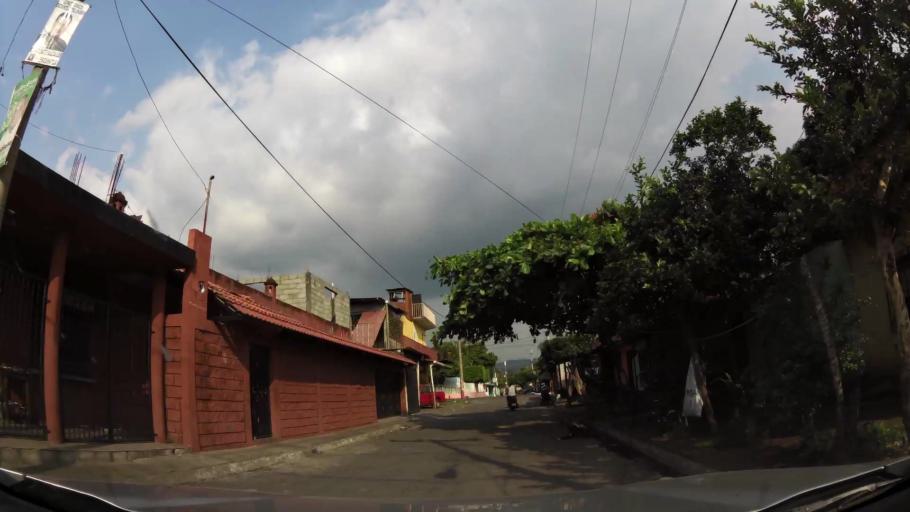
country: GT
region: Escuintla
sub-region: Municipio de Escuintla
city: Escuintla
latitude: 14.3142
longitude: -90.7960
